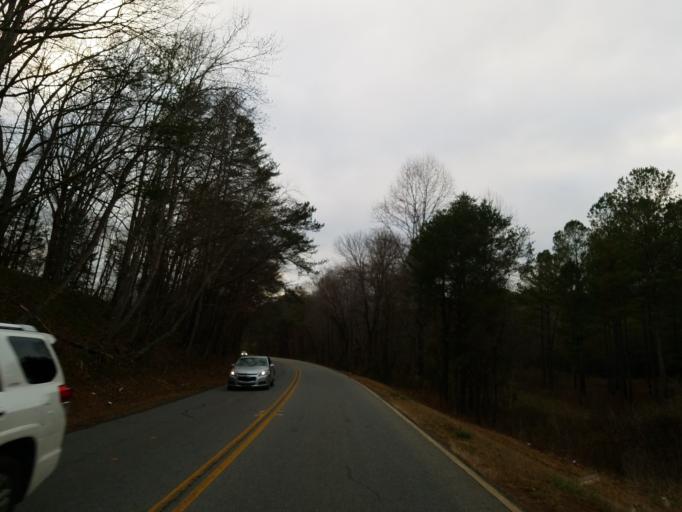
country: US
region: Georgia
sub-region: Bartow County
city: Rydal
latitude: 34.3494
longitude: -84.6756
